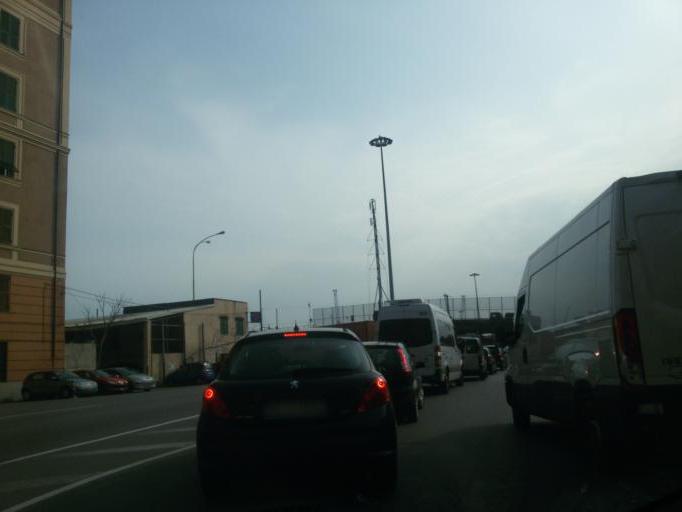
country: IT
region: Liguria
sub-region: Provincia di Genova
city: San Teodoro
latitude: 44.4107
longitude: 8.8867
